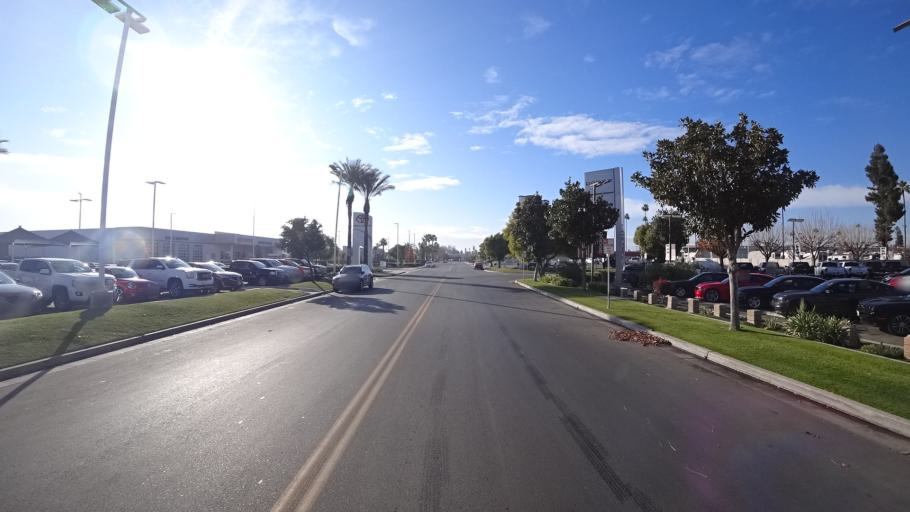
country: US
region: California
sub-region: Kern County
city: Greenfield
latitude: 35.3036
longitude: -119.0356
